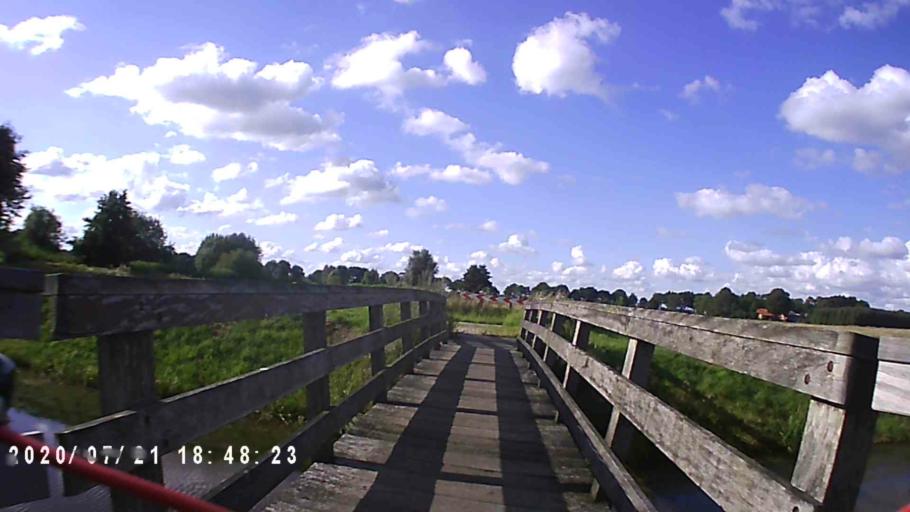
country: NL
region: Groningen
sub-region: Gemeente Hoogezand-Sappemeer
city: Hoogezand
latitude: 53.2162
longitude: 6.7480
